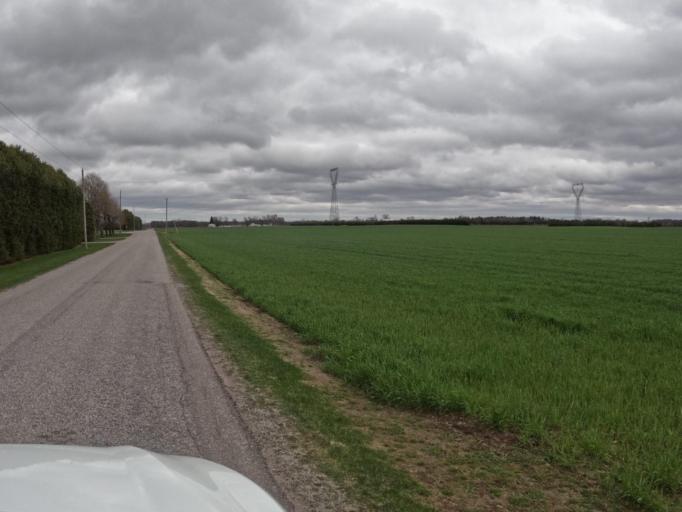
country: CA
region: Ontario
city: Norfolk County
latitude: 42.9621
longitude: -80.4276
